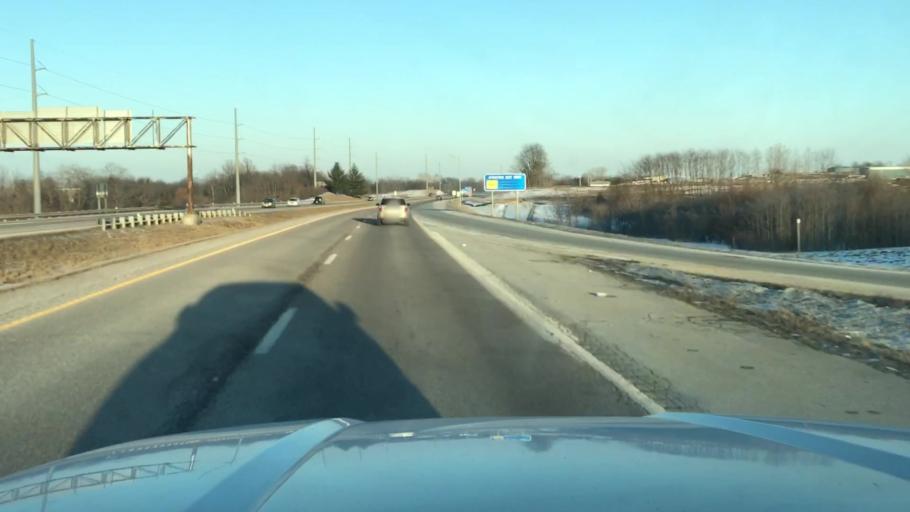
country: US
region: Missouri
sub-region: Buchanan County
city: Saint Joseph
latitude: 39.7503
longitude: -94.7865
